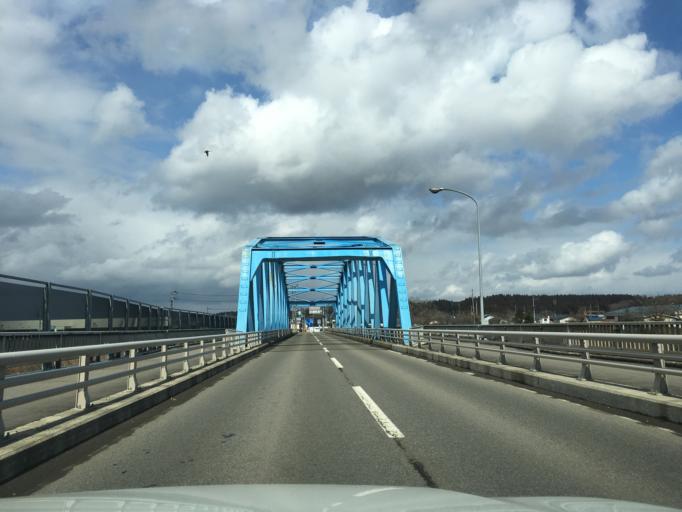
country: JP
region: Akita
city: Takanosu
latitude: 40.1206
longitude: 140.3676
